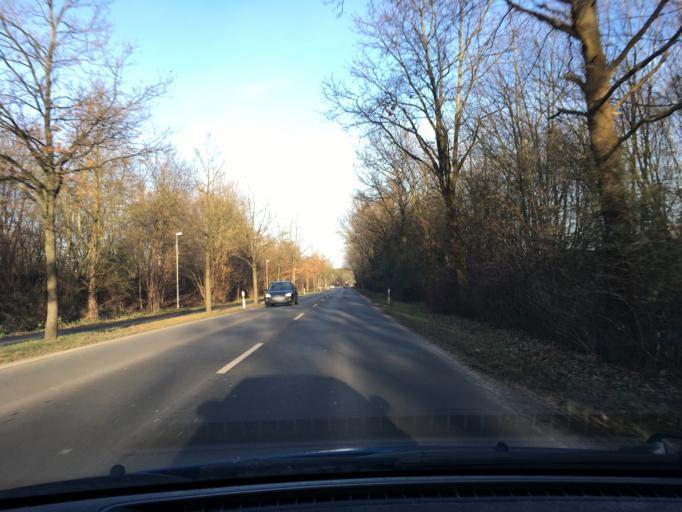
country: DE
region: Lower Saxony
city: Winsen
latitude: 53.3558
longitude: 10.2252
